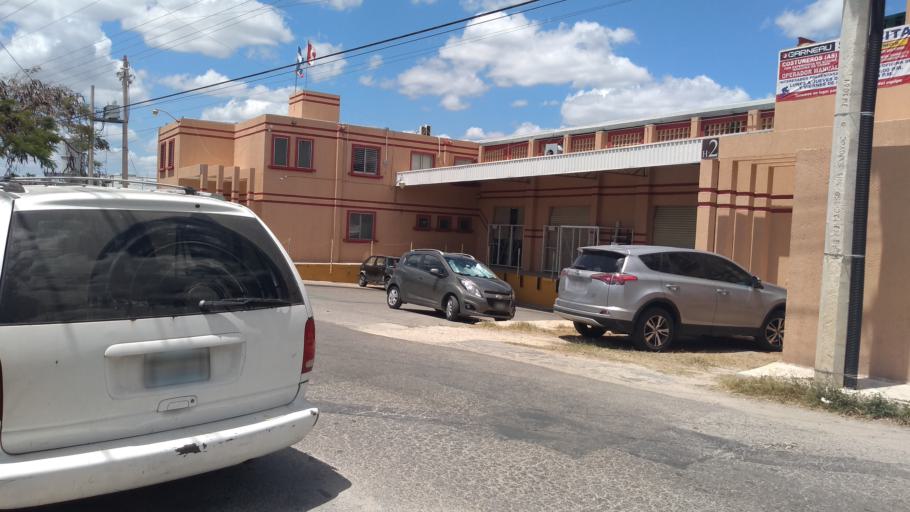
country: MX
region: Yucatan
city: Itzincab Palomeque
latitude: 20.9291
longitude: -89.6727
